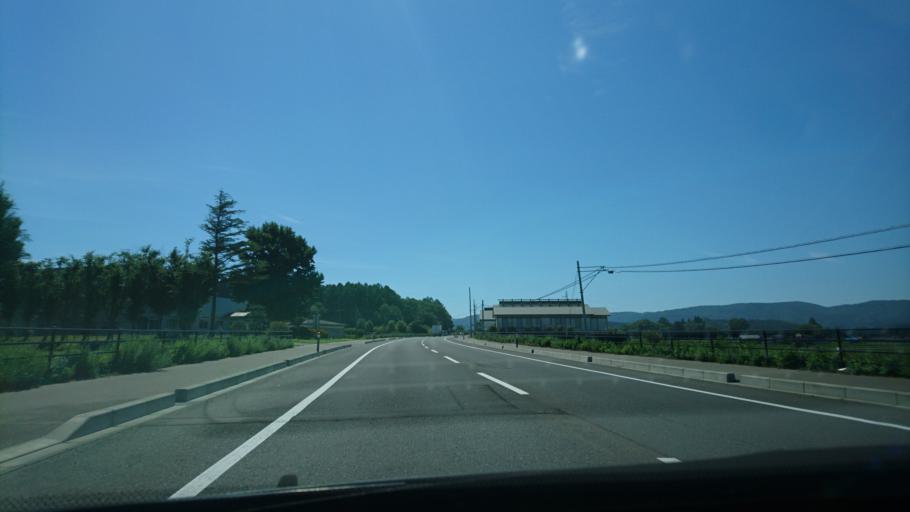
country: JP
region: Iwate
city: Tono
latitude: 39.3072
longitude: 141.5733
